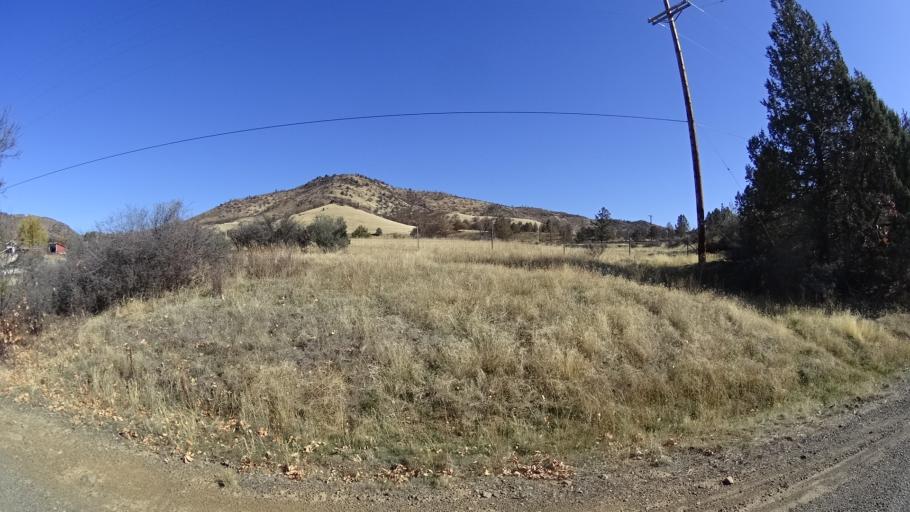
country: US
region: California
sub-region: Siskiyou County
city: Yreka
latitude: 41.9456
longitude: -122.5859
